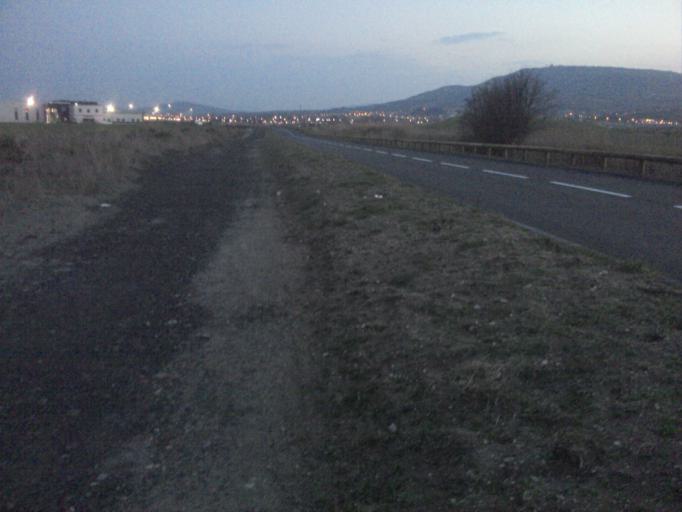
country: FR
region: Auvergne
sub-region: Departement du Puy-de-Dome
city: Perignat-les-Sarlieve
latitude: 45.7524
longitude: 3.1508
